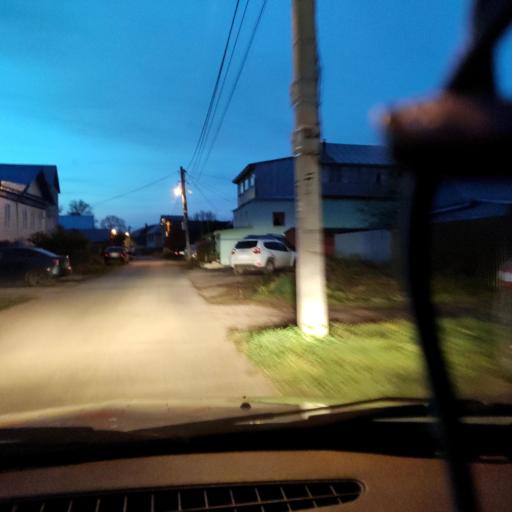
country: RU
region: Bashkortostan
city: Ufa
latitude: 54.7253
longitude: 55.9032
